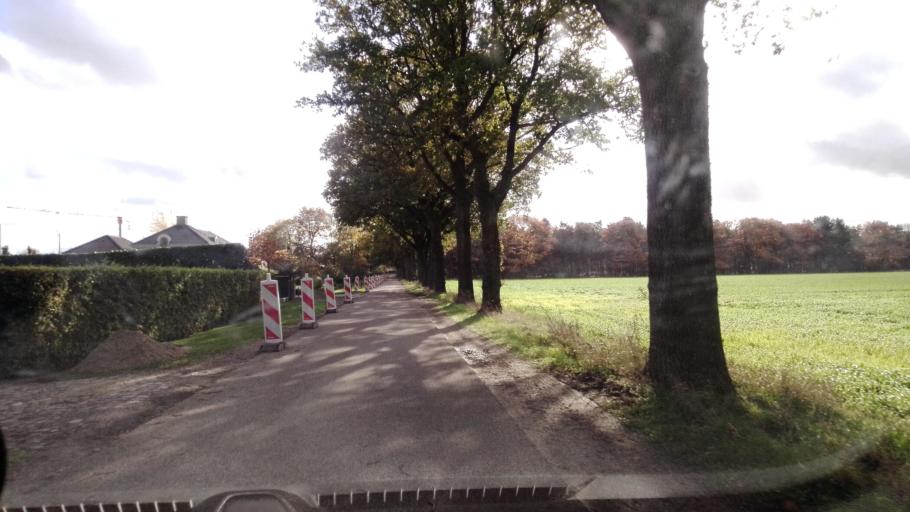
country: NL
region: Limburg
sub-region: Gemeente Venray
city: Venray
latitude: 51.4858
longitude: 5.9159
